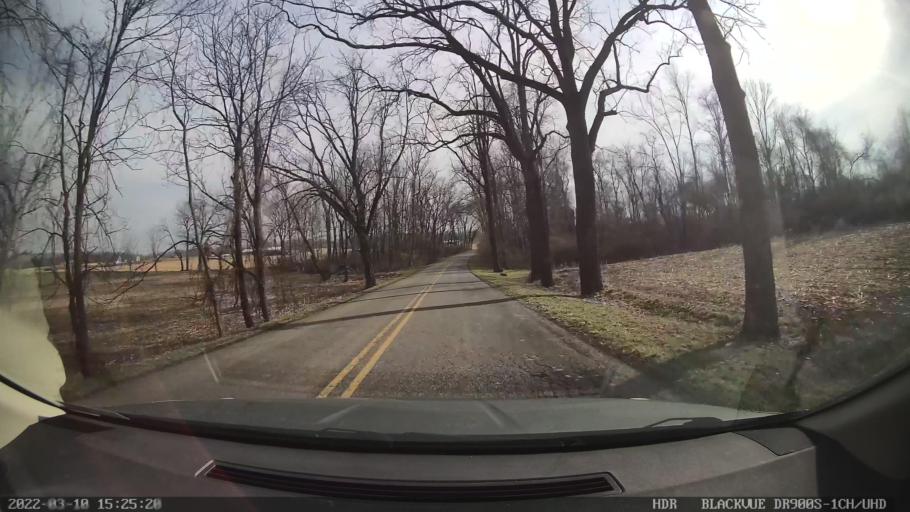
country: US
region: Pennsylvania
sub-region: Berks County
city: Oley
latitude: 40.3559
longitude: -75.7877
